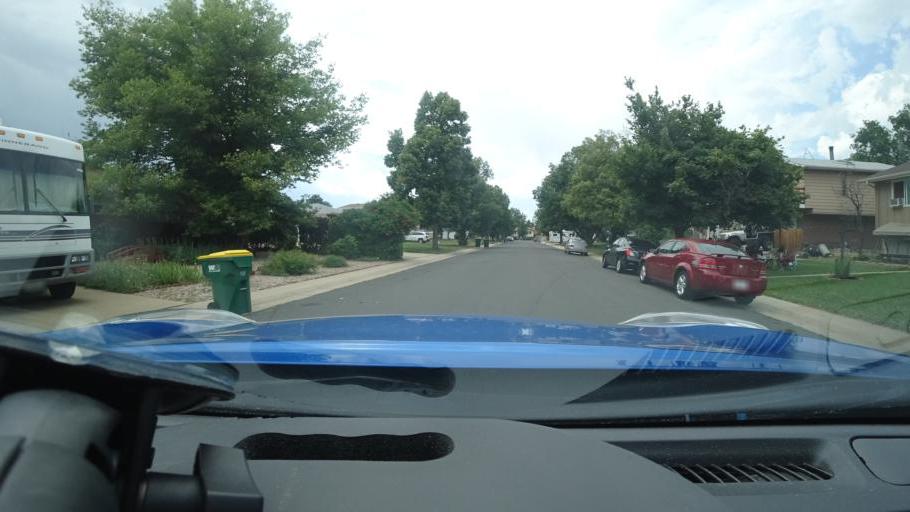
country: US
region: Colorado
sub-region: Adams County
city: Aurora
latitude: 39.7212
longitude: -104.8293
